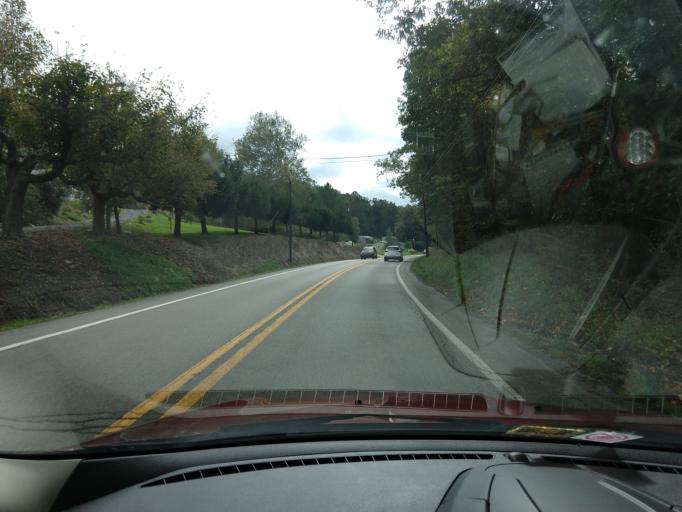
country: US
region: West Virginia
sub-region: Barbour County
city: Belington
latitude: 39.0028
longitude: -79.9376
